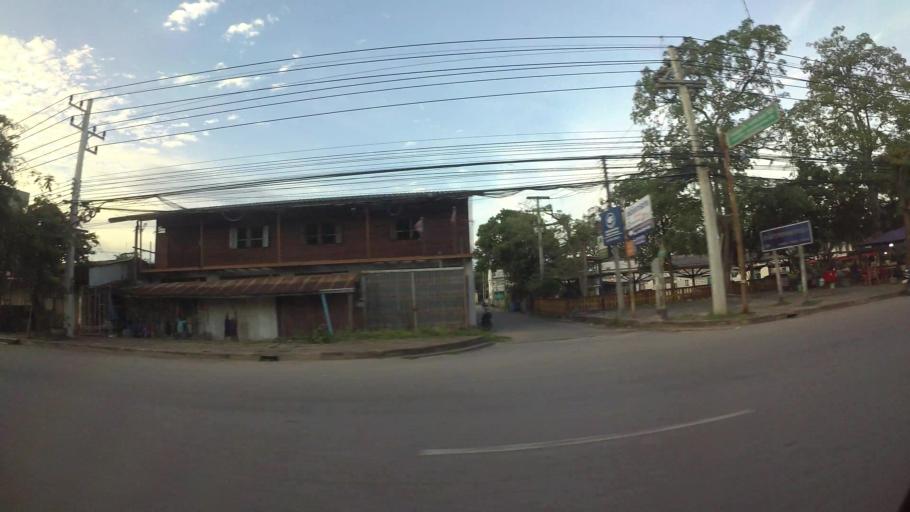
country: TH
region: Rayong
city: Rayong
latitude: 12.6764
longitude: 101.2884
